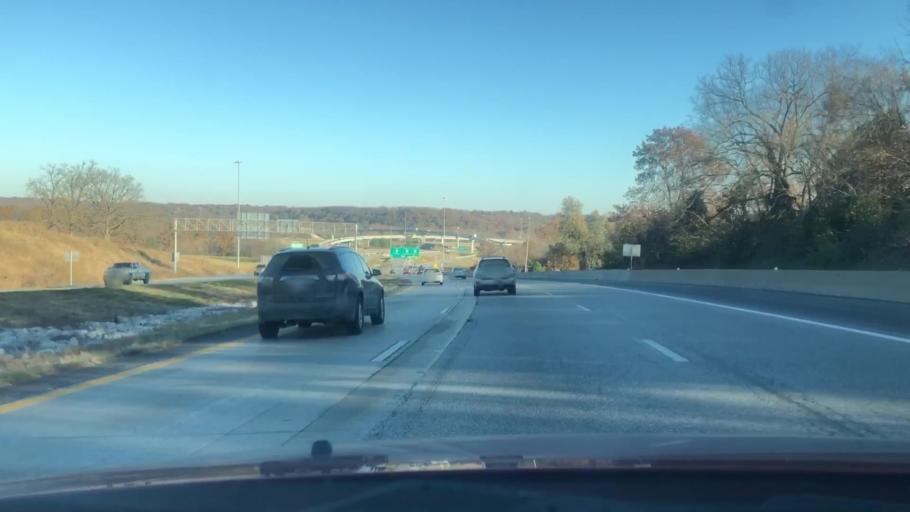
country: US
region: Missouri
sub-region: Greene County
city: Springfield
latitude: 37.1312
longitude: -93.2422
